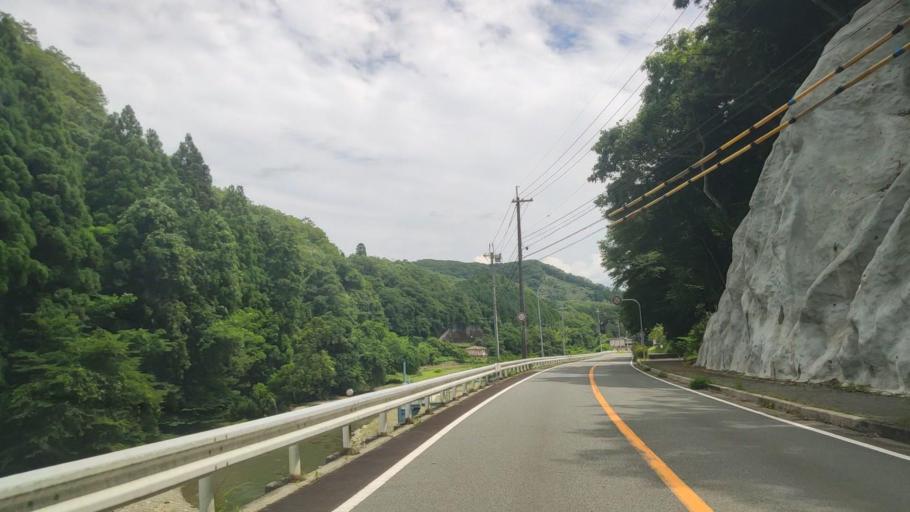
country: JP
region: Hyogo
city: Yamazakicho-nakabirose
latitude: 35.0650
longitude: 134.3628
